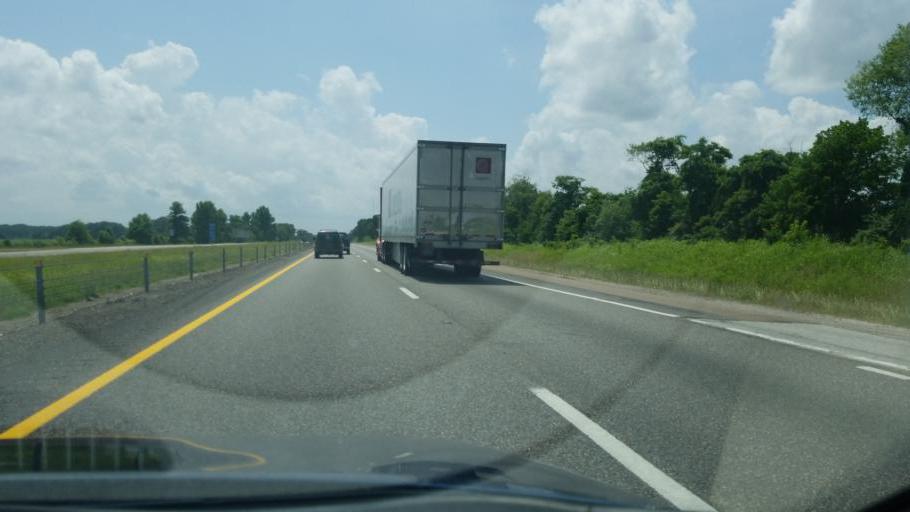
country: US
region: Tennessee
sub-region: Madison County
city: Jackson
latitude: 35.6410
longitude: -88.9223
